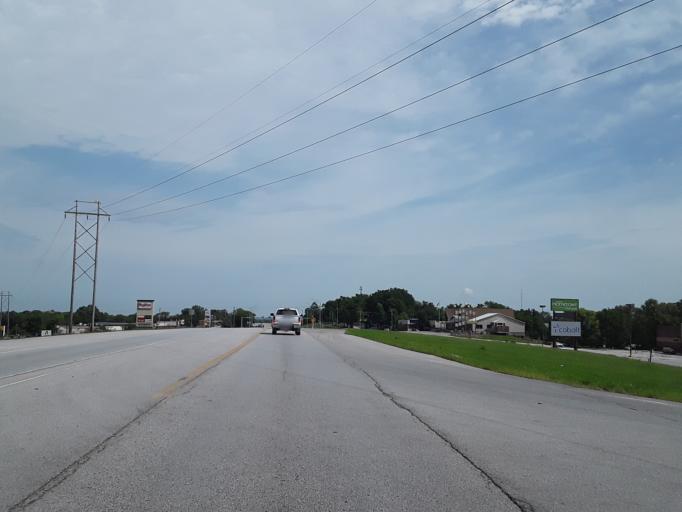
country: US
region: Nebraska
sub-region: Cass County
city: Plattsmouth
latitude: 41.0094
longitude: -95.9087
